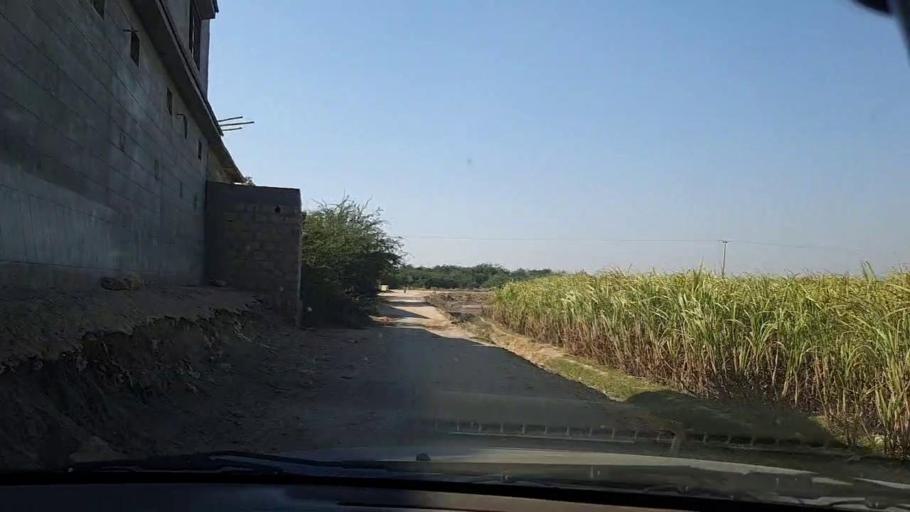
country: PK
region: Sindh
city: Thatta
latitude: 24.6036
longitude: 68.0519
